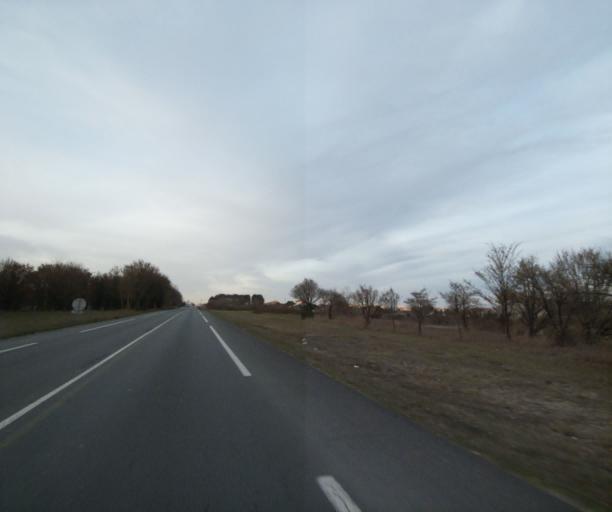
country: FR
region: Poitou-Charentes
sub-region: Departement de la Charente-Maritime
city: Saintes
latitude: 45.7388
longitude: -0.6603
